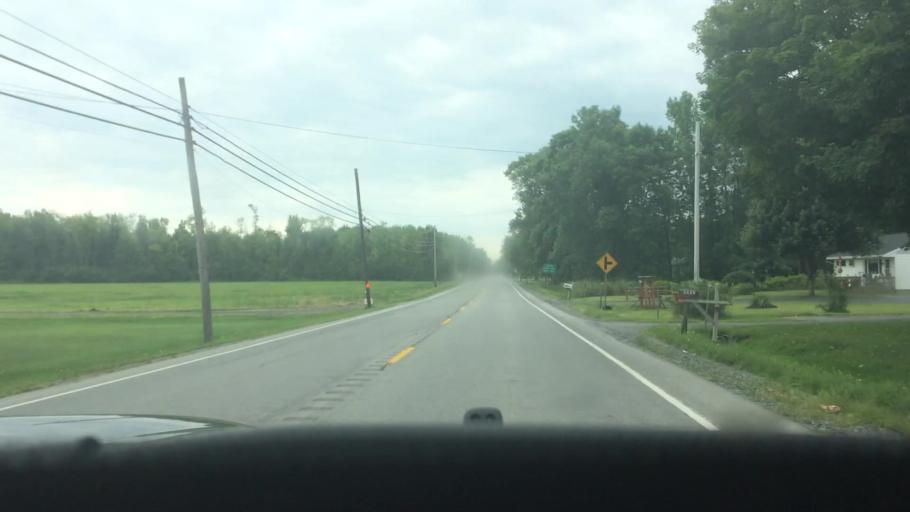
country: US
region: New York
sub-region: St. Lawrence County
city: Ogdensburg
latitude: 44.6546
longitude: -75.4470
